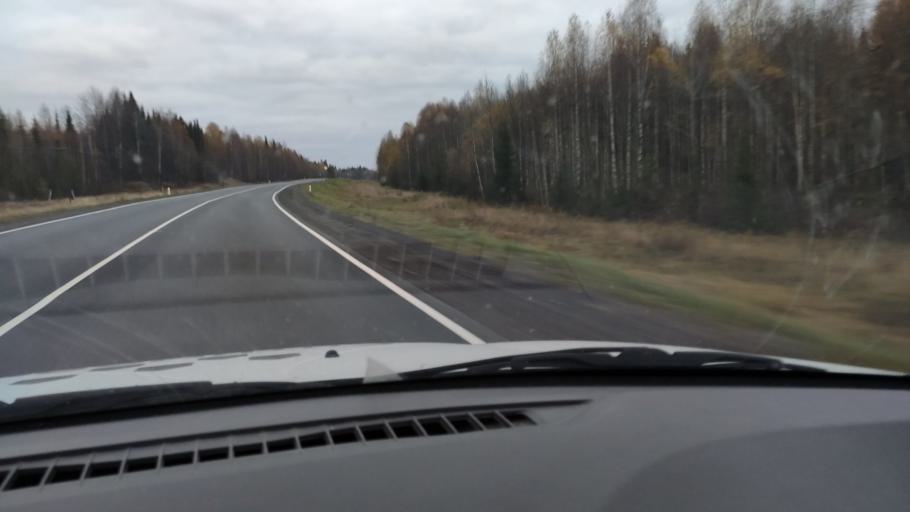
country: RU
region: Kirov
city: Lesnyye Polyany
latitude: 58.8261
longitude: 52.6109
